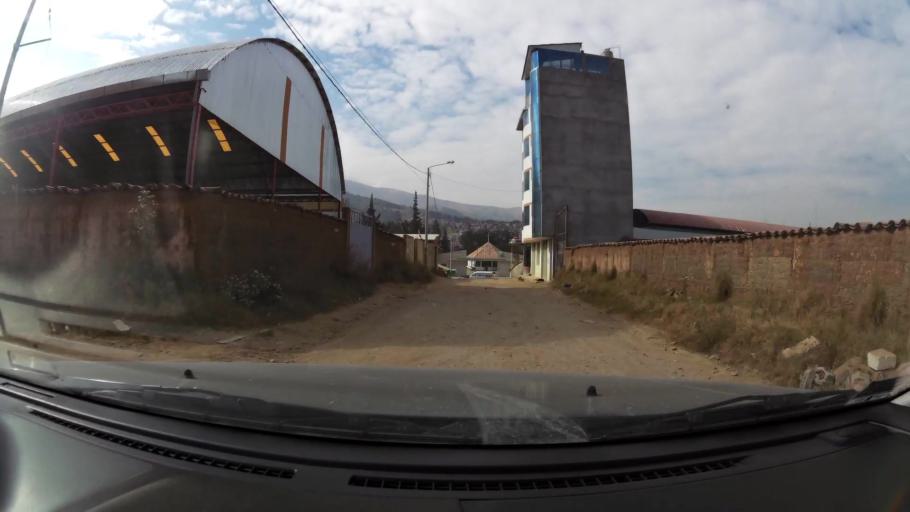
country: PE
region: Junin
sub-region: Provincia de Huancayo
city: Huancayo
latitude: -12.0536
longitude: -75.1964
